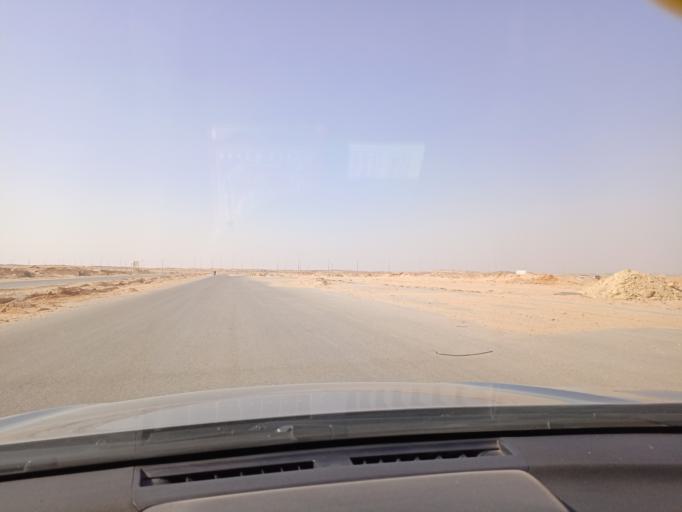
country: EG
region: Muhafazat al Qalyubiyah
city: Al Khankah
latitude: 30.0405
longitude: 31.7153
